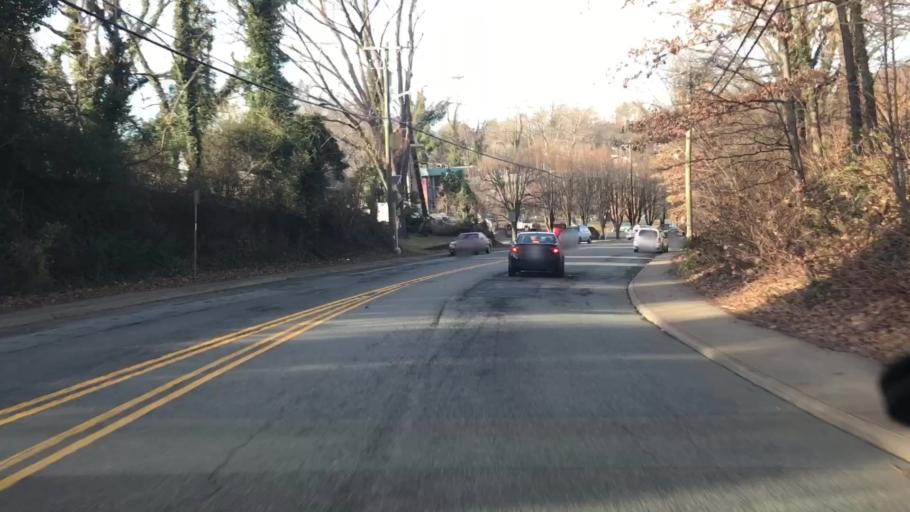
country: US
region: Virginia
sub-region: City of Charlottesville
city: Charlottesville
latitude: 38.0401
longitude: -78.4919
